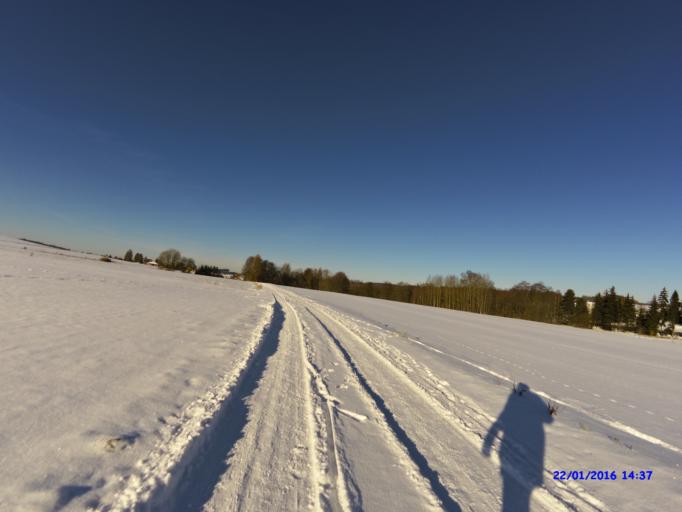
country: DE
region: Thuringia
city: Tanna
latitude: 50.4891
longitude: 11.8656
